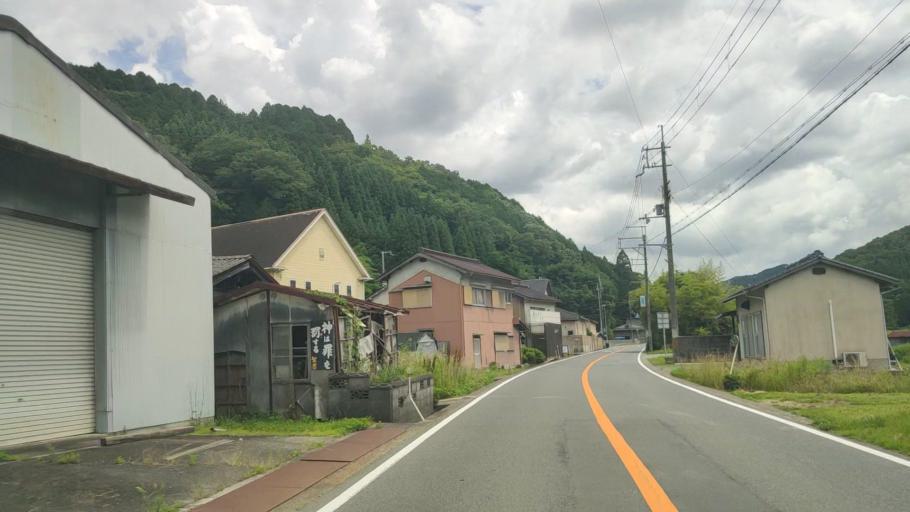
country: JP
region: Hyogo
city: Yamazakicho-nakabirose
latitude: 34.9741
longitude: 134.4462
